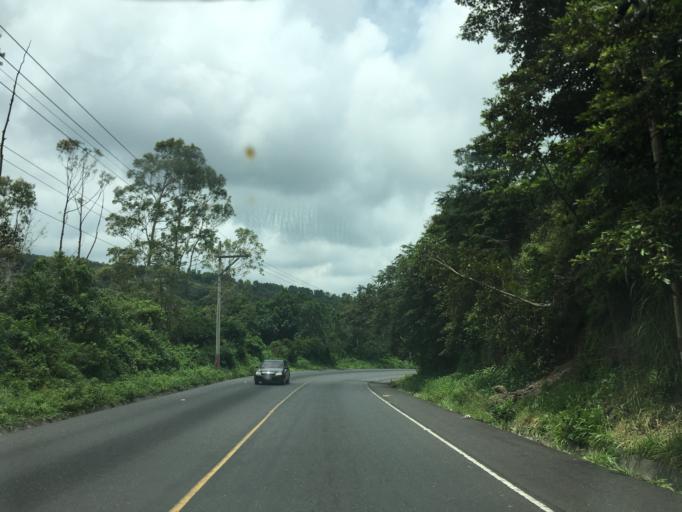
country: GT
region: Sacatepequez
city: Alotenango
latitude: 14.4531
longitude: -90.8113
